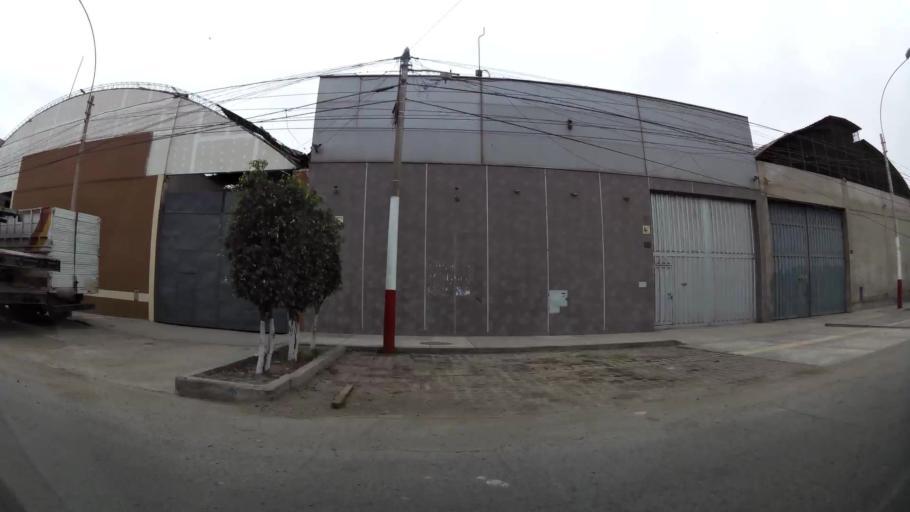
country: PE
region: Callao
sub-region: Callao
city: Callao
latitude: -12.0529
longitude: -77.1171
